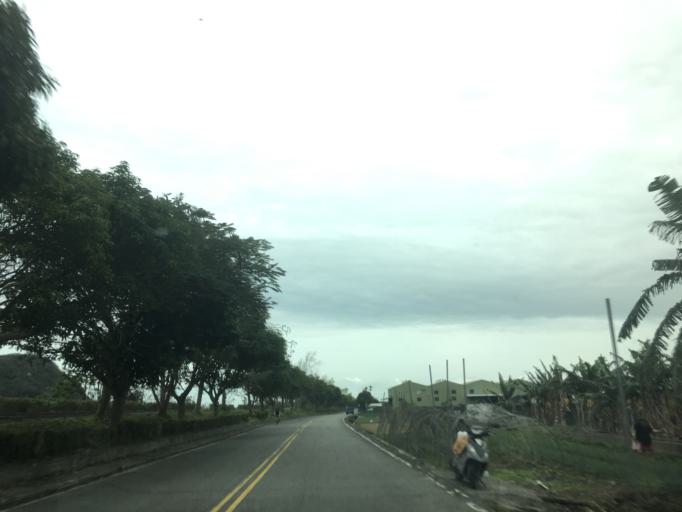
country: TW
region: Taiwan
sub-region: Taitung
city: Taitung
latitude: 22.8036
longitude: 121.1344
